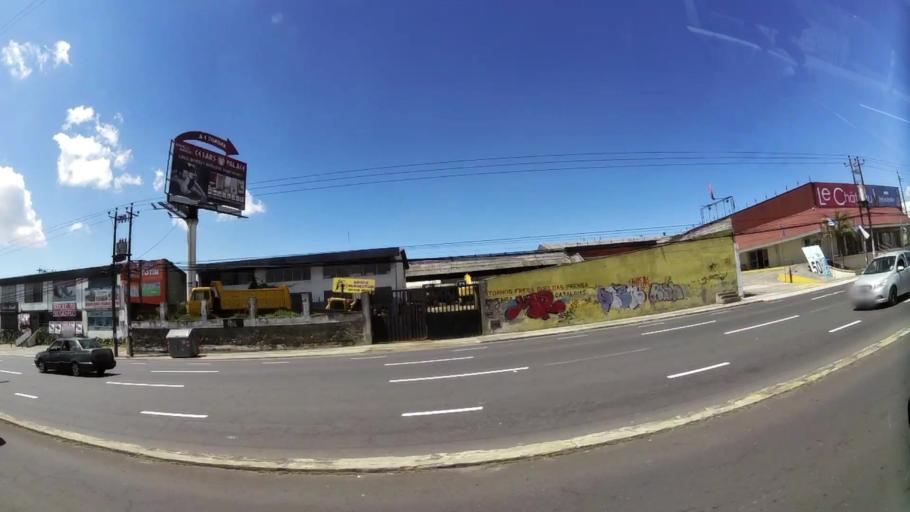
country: EC
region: Pichincha
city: Quito
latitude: -0.1069
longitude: -78.4772
